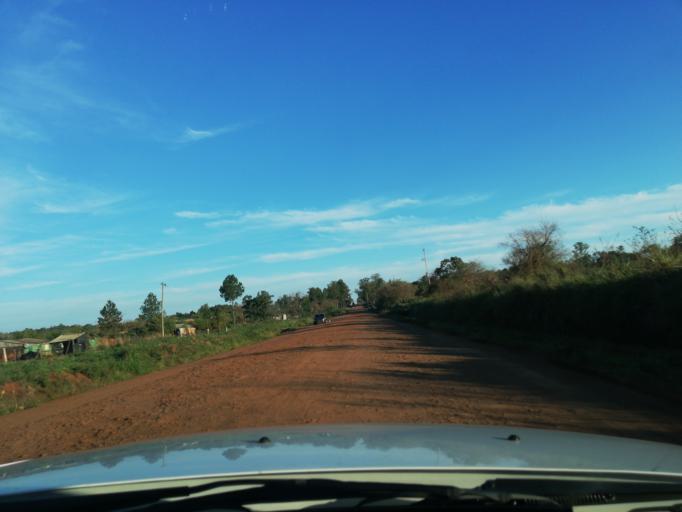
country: AR
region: Misiones
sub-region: Departamento de Capital
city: Posadas
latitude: -27.4723
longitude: -55.9708
